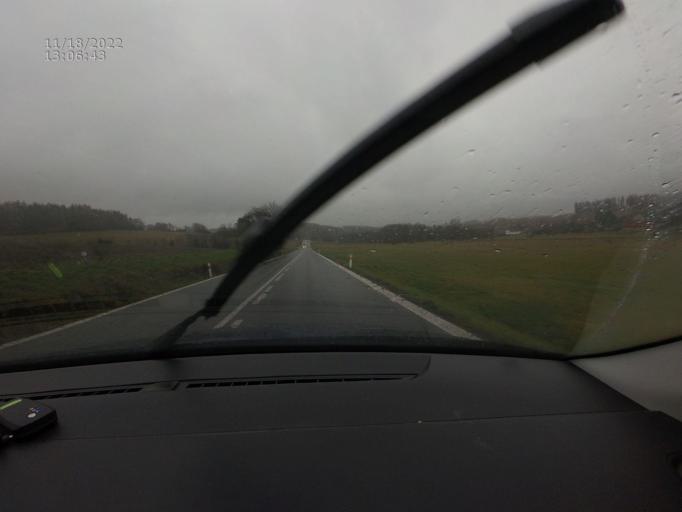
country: CZ
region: Plzensky
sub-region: Okres Klatovy
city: Planice
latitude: 49.3343
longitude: 13.4974
